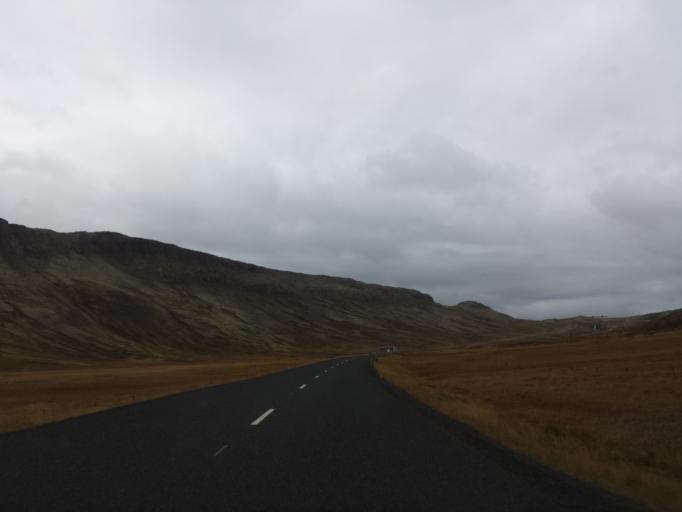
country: IS
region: West
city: Stykkisholmur
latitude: 64.8914
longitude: -22.8324
